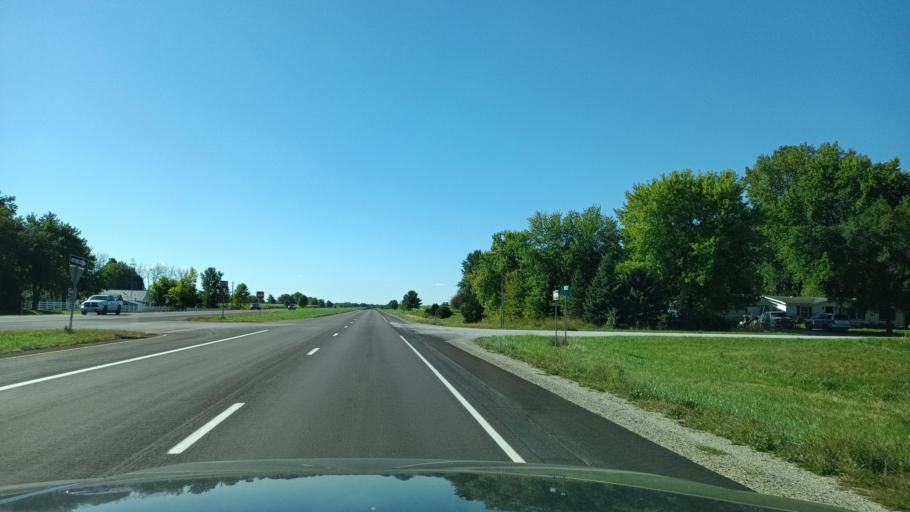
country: US
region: Iowa
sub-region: Lee County
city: Keokuk
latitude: 40.4731
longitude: -91.4447
